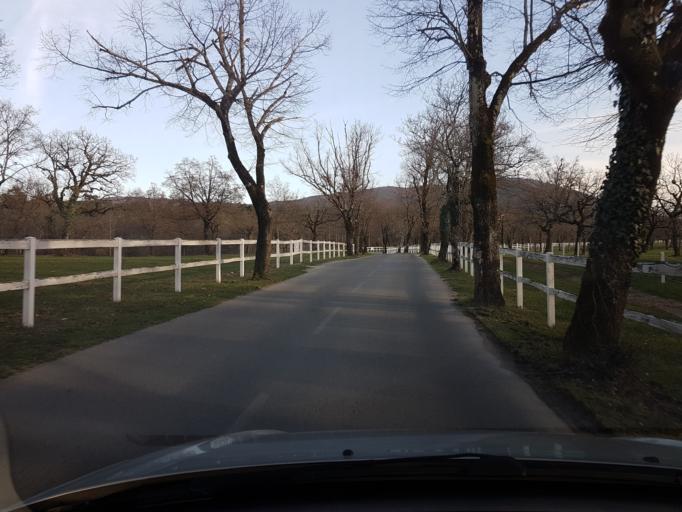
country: SI
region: Sezana
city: Sezana
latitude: 45.6642
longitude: 13.8906
